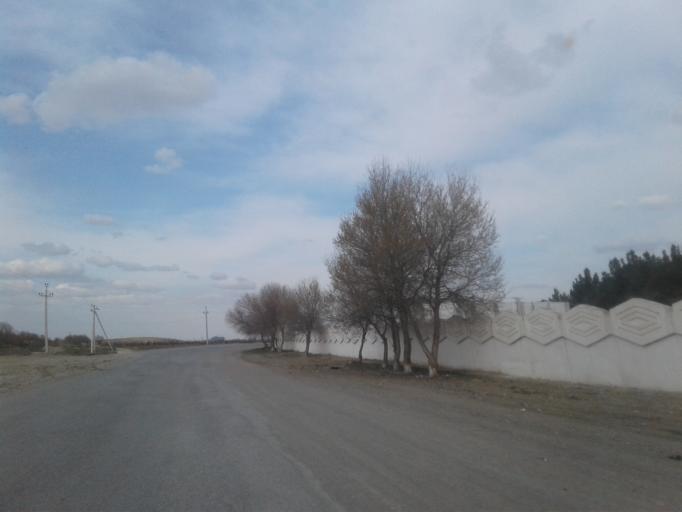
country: TM
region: Ahal
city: Abadan
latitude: 38.1231
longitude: 58.3458
